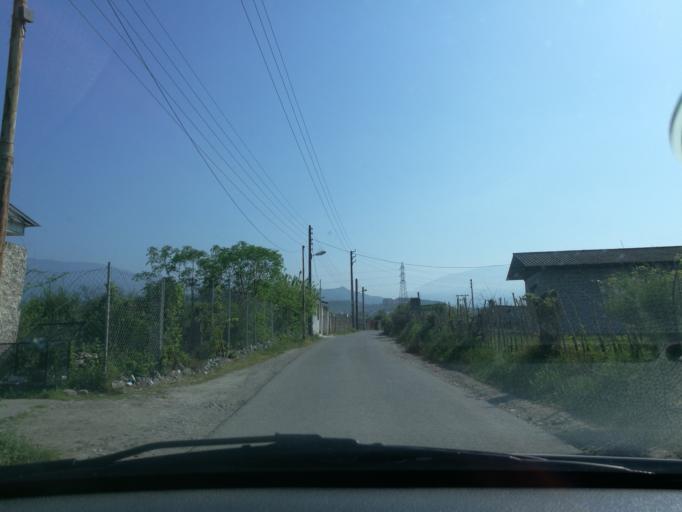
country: IR
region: Mazandaran
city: Chalus
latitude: 36.6622
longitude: 51.4386
